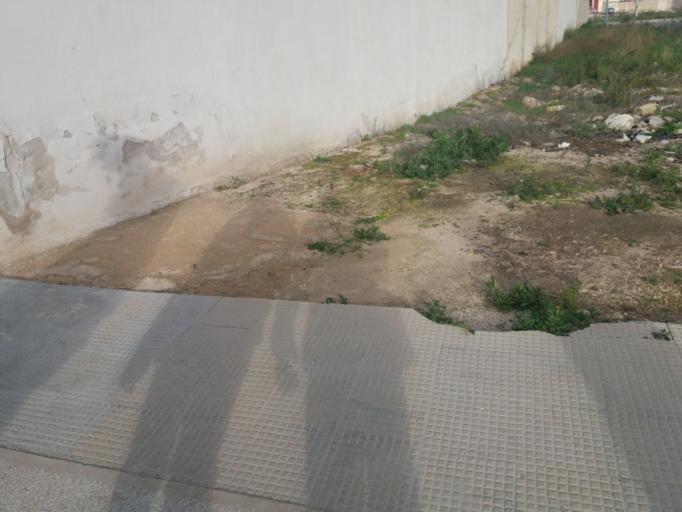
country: IT
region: Apulia
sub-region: Provincia di Barletta - Andria - Trani
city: Andria
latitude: 41.2416
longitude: 16.2890
